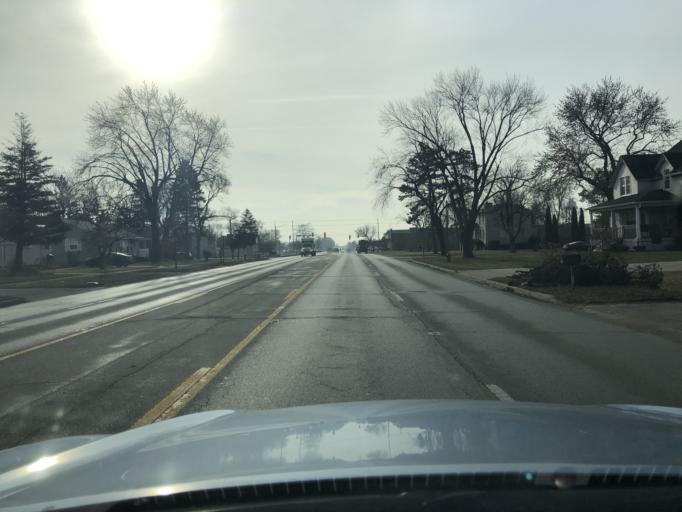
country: US
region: Illinois
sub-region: Cook County
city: Des Plaines
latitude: 42.0254
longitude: -87.9091
